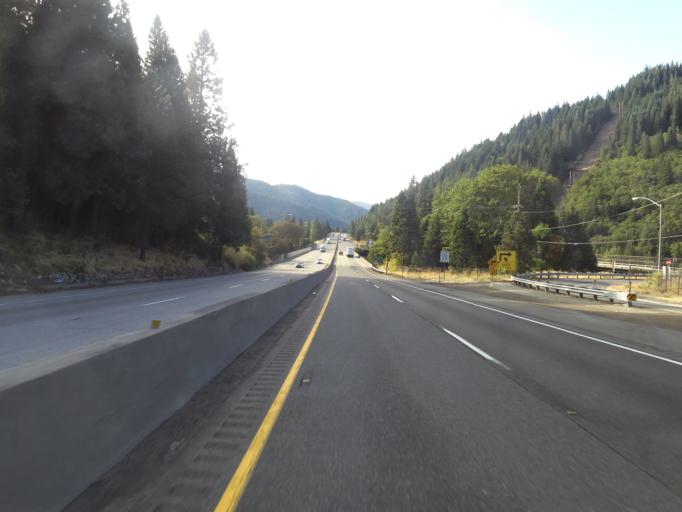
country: US
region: California
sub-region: Siskiyou County
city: Dunsmuir
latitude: 41.2226
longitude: -122.2756
